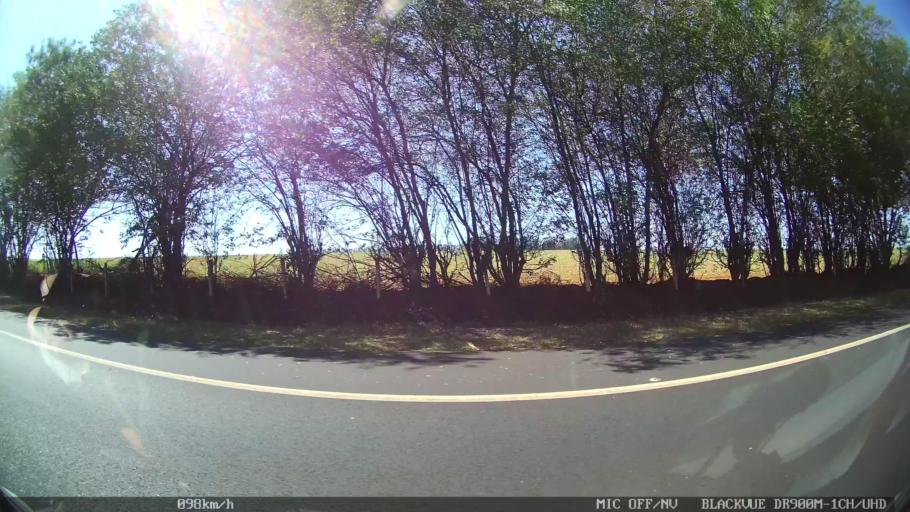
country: BR
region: Sao Paulo
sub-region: Batatais
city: Batatais
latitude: -20.7439
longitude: -47.5312
